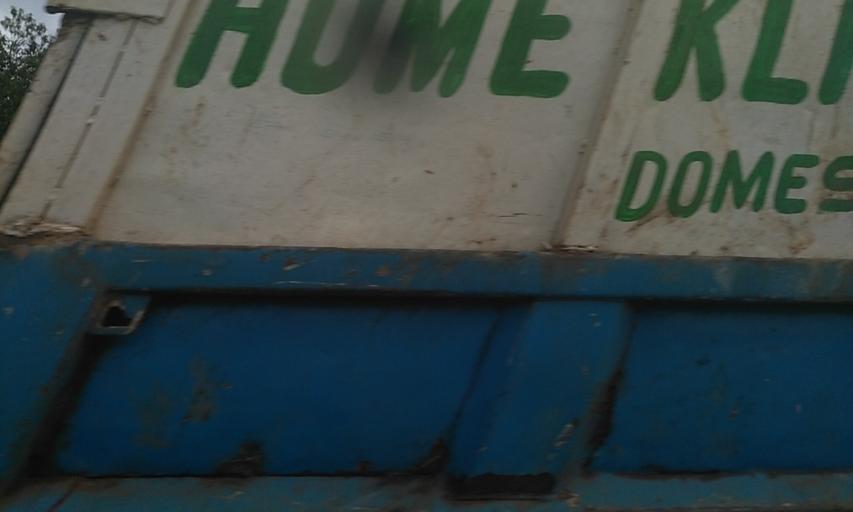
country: UG
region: Central Region
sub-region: Wakiso District
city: Bweyogerere
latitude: 0.3935
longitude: 32.6624
